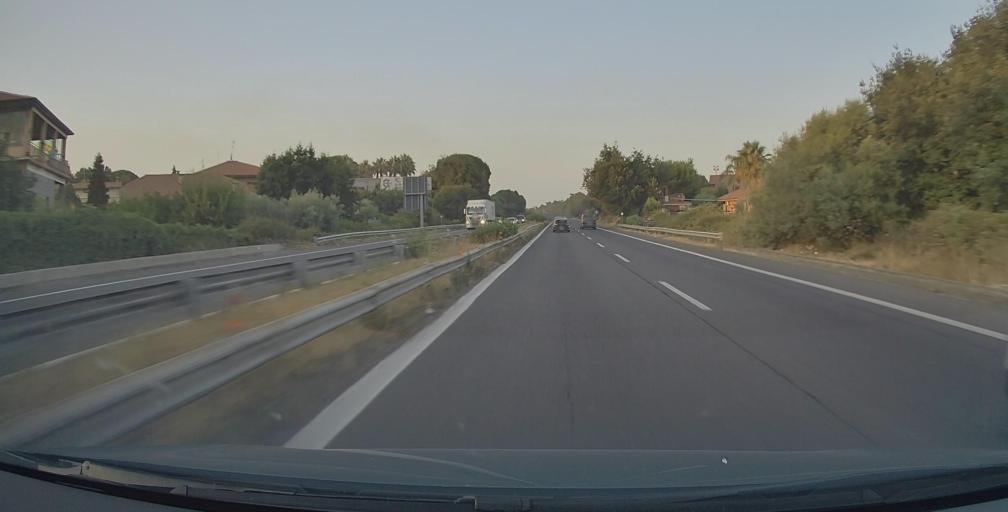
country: IT
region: Sicily
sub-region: Catania
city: Maugeri
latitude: 37.5783
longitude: 15.1155
